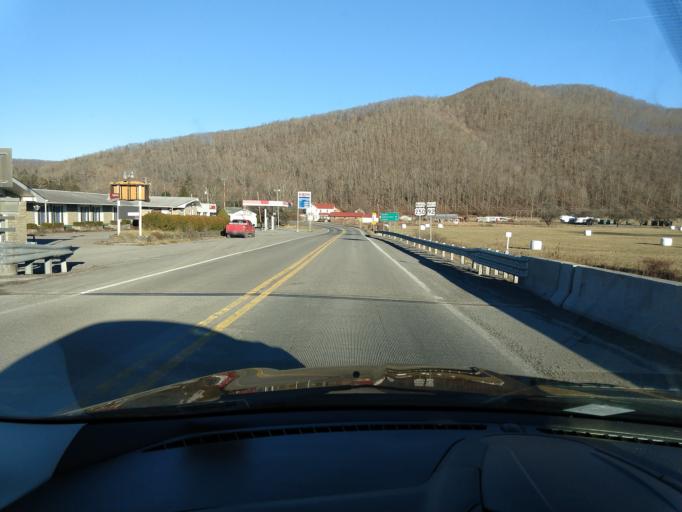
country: US
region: Virginia
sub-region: Highland County
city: Monterey
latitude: 38.5403
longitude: -79.7808
